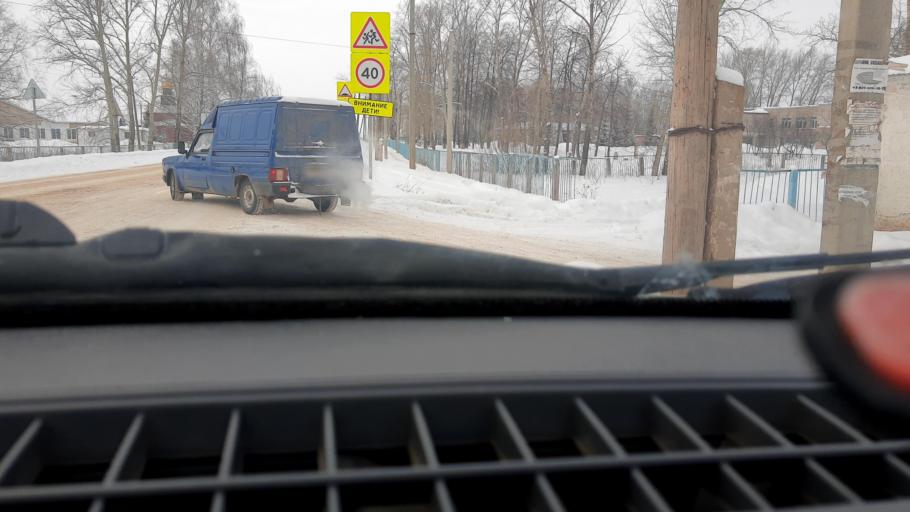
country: RU
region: Bashkortostan
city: Davlekanovo
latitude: 54.5795
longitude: 54.9366
